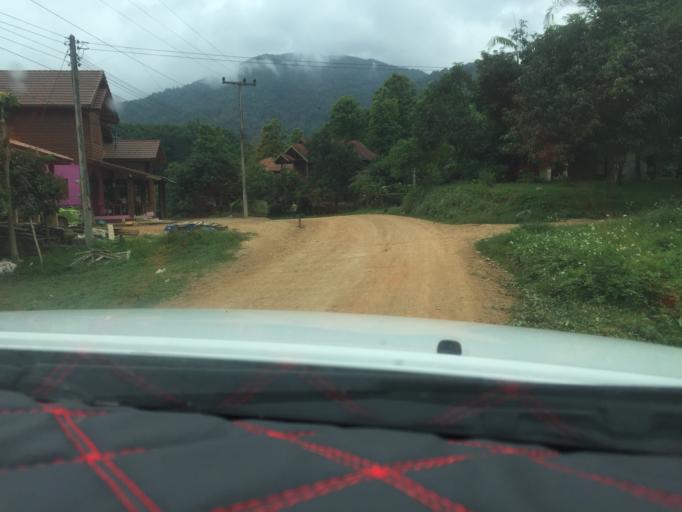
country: TH
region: Phayao
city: Phu Sang
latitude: 19.6895
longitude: 100.5020
